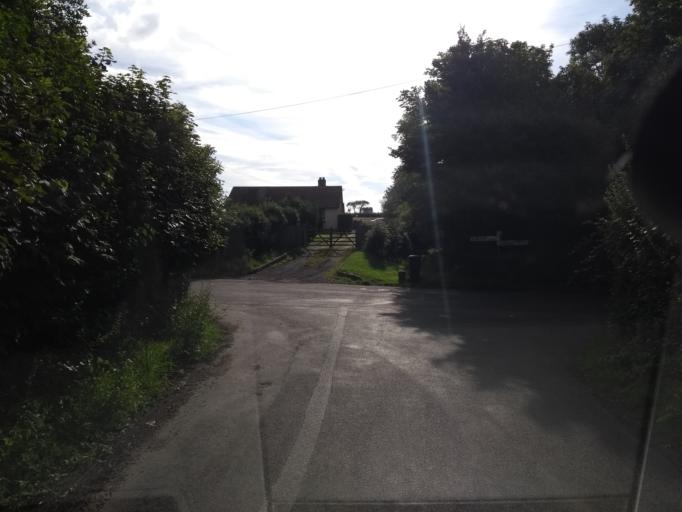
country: GB
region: England
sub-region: Somerset
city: Axbridge
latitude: 51.2637
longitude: -2.8530
